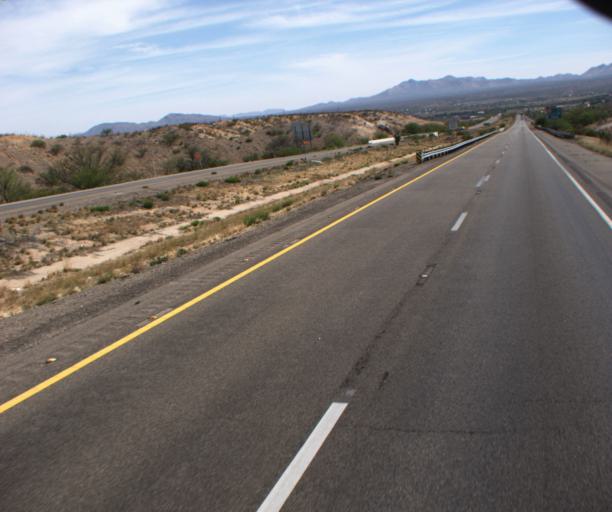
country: US
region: Arizona
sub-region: Cochise County
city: Whetstone
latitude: 31.9722
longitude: -110.3255
